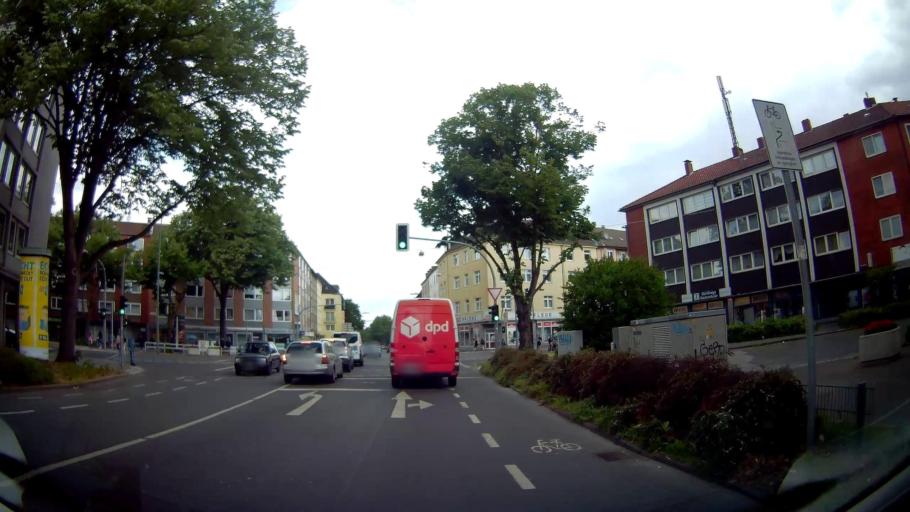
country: DE
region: North Rhine-Westphalia
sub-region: Regierungsbezirk Munster
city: Gelsenkirchen
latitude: 51.5150
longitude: 7.1029
